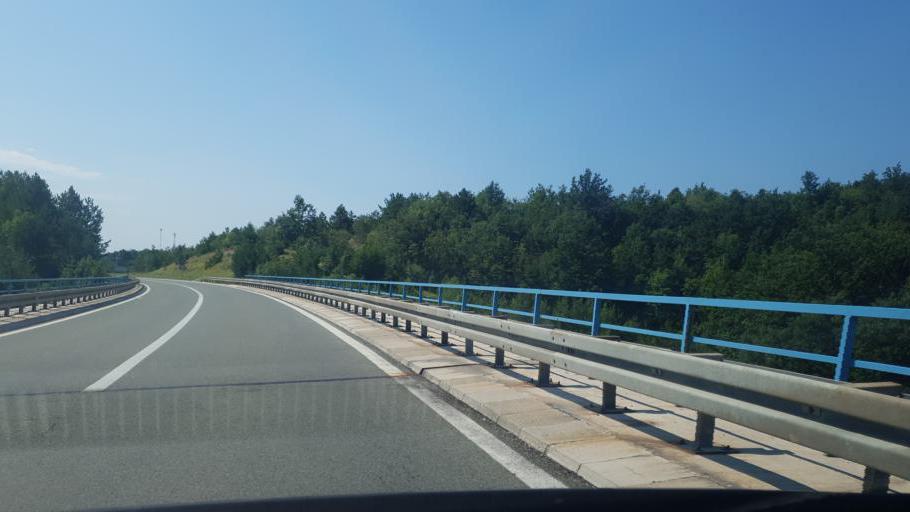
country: HR
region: Istarska
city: Buzet
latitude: 45.3291
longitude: 14.0739
